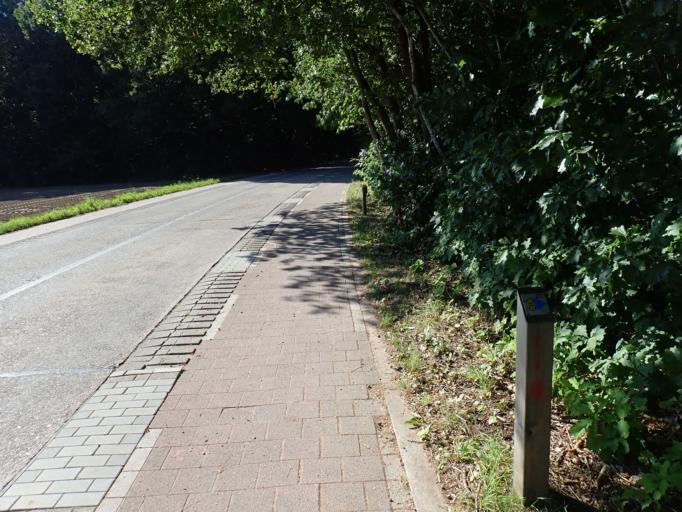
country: BE
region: Flanders
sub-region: Provincie Antwerpen
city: Olen
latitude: 51.1384
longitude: 4.8927
